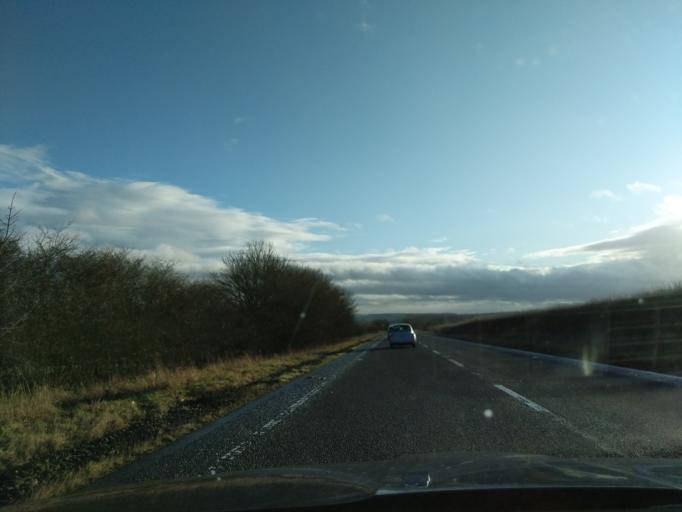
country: GB
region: England
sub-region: Northumberland
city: Alnwick
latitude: 55.4409
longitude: -1.6966
